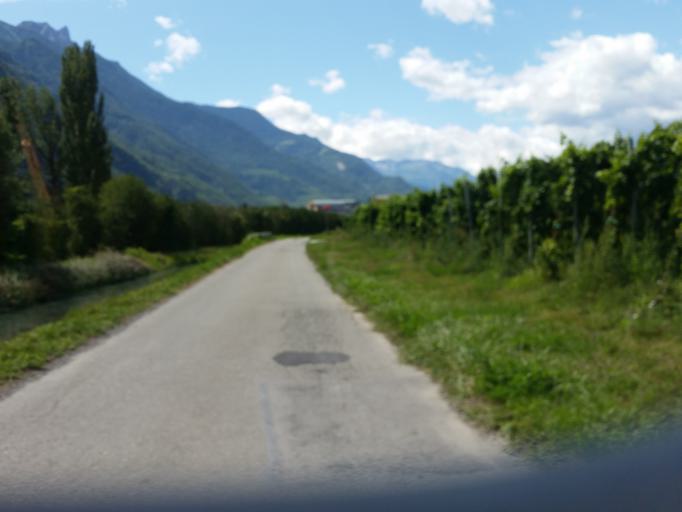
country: CH
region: Valais
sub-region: Martigny District
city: Riddes
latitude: 46.1802
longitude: 7.2327
